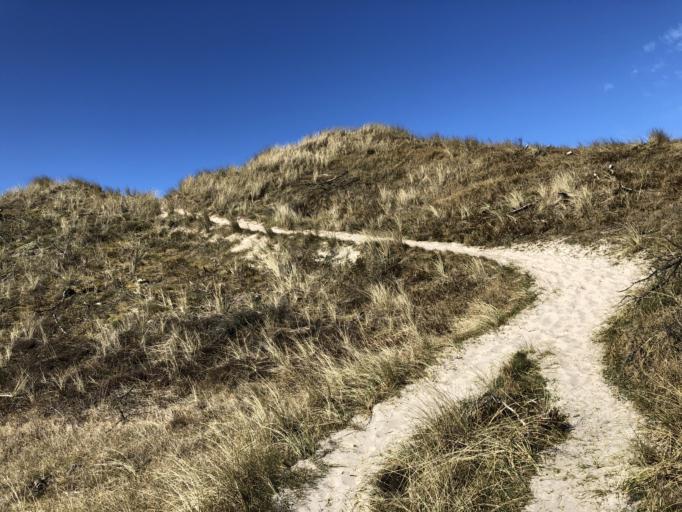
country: DK
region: Central Jutland
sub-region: Holstebro Kommune
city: Ulfborg
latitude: 56.3053
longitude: 8.1265
